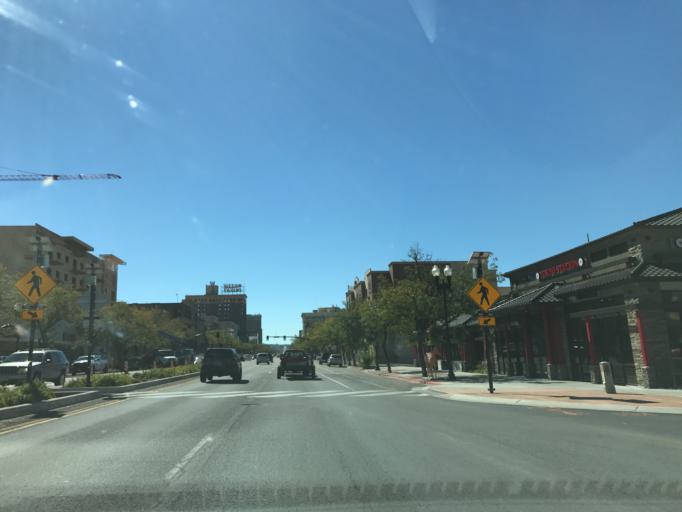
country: US
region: Utah
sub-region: Weber County
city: Ogden
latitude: 41.2262
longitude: -111.9704
